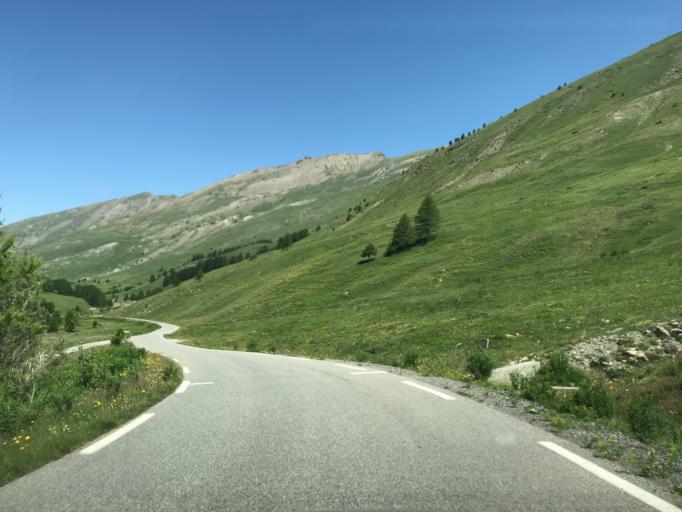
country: IT
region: Piedmont
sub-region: Provincia di Cuneo
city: Pontechianale
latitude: 44.7102
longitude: 6.9229
